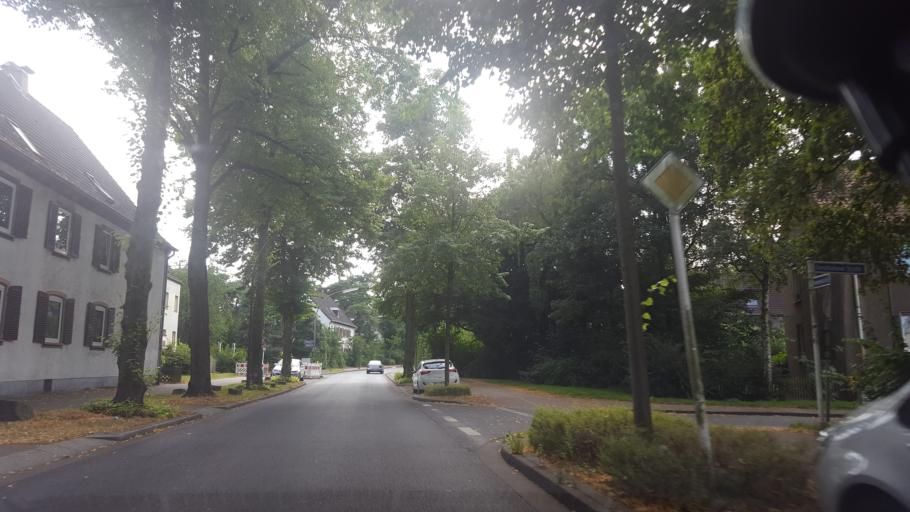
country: DE
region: North Rhine-Westphalia
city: Marl
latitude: 51.6711
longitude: 7.1093
